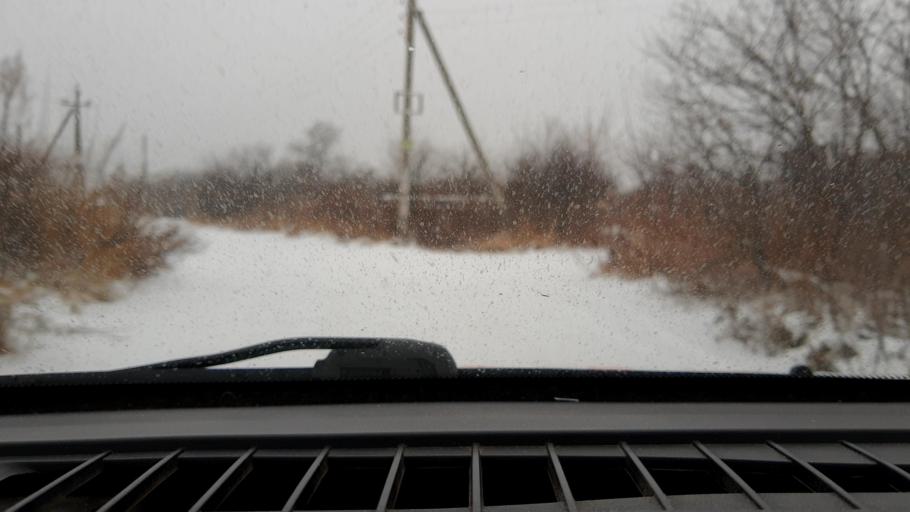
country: RU
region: Nizjnij Novgorod
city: Nizhniy Novgorod
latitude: 56.2365
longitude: 43.9914
